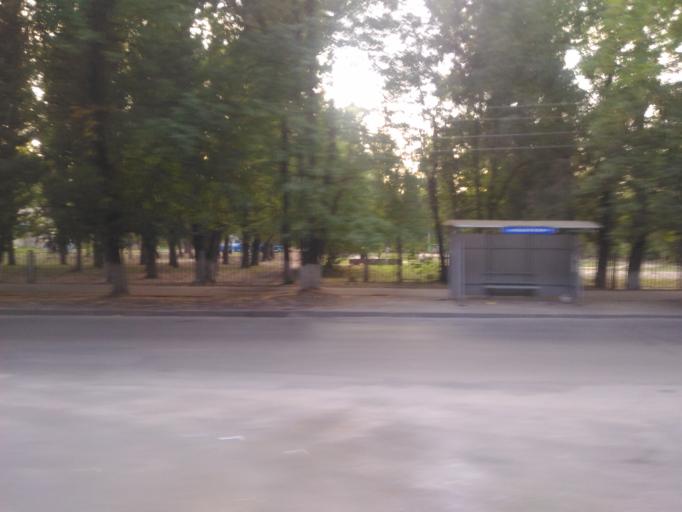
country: RU
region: Ulyanovsk
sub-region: Ulyanovskiy Rayon
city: Ulyanovsk
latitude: 54.3005
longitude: 48.3216
